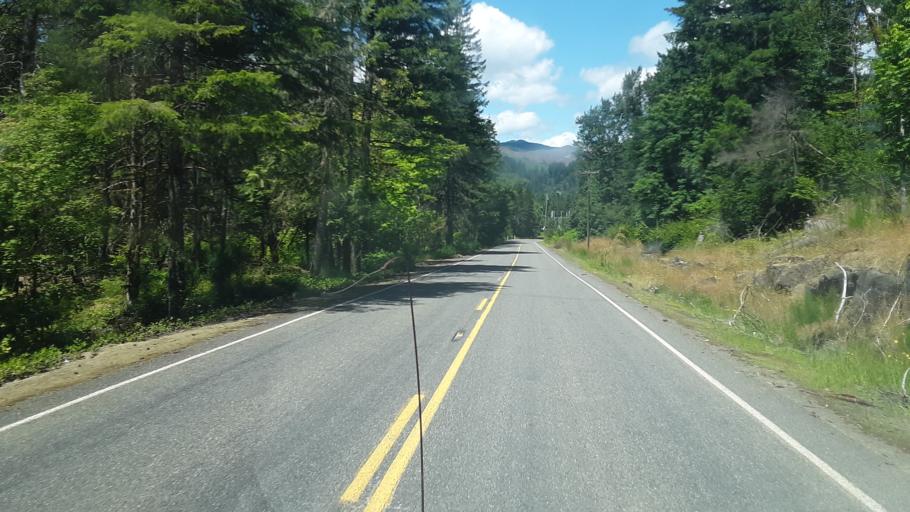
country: US
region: Washington
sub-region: Clark County
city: Amboy
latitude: 46.0576
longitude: -122.2557
